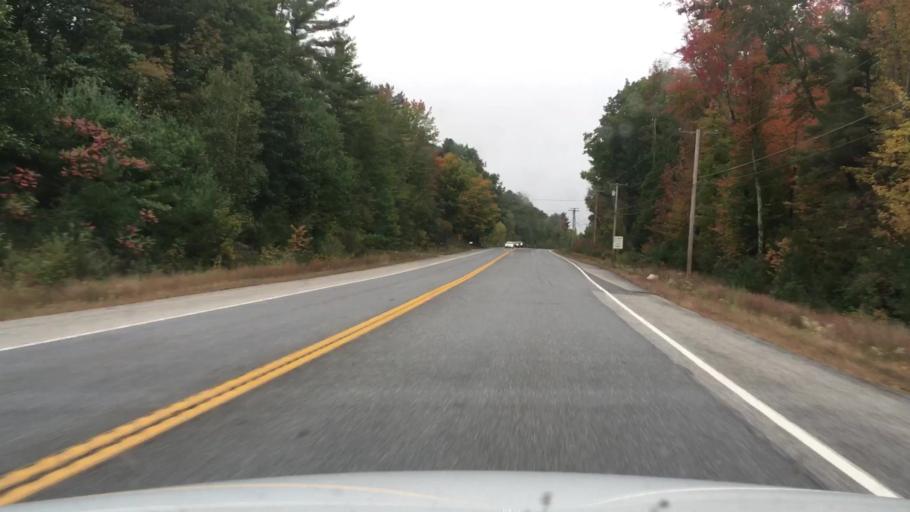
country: US
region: Maine
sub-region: Cumberland County
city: New Gloucester
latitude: 43.9727
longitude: -70.3643
